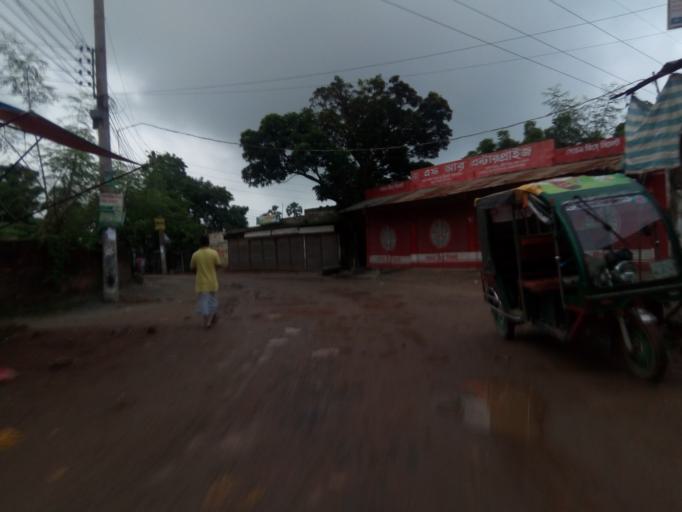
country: BD
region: Dhaka
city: Tungi
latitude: 23.8528
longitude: 90.4322
